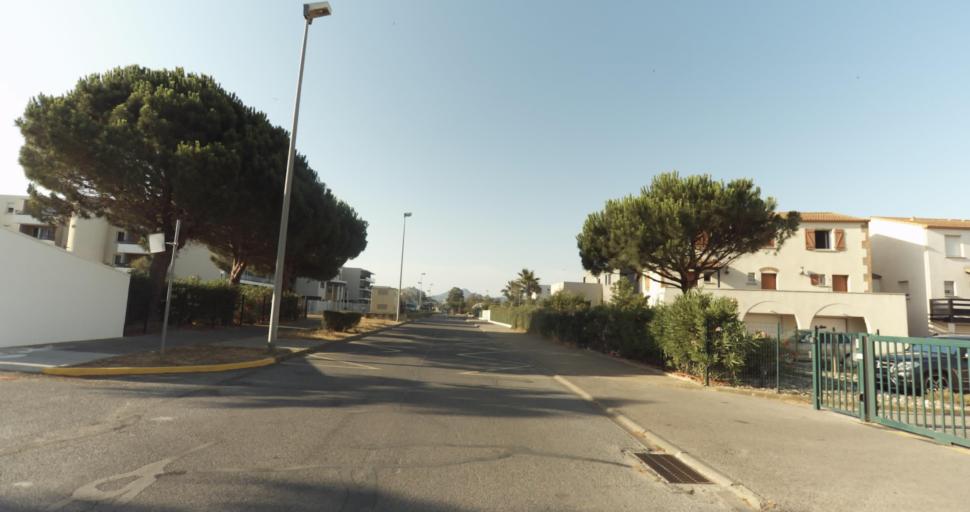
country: FR
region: Languedoc-Roussillon
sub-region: Departement des Pyrenees-Orientales
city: Saint-Cyprien-Plage
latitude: 42.6051
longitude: 3.0393
